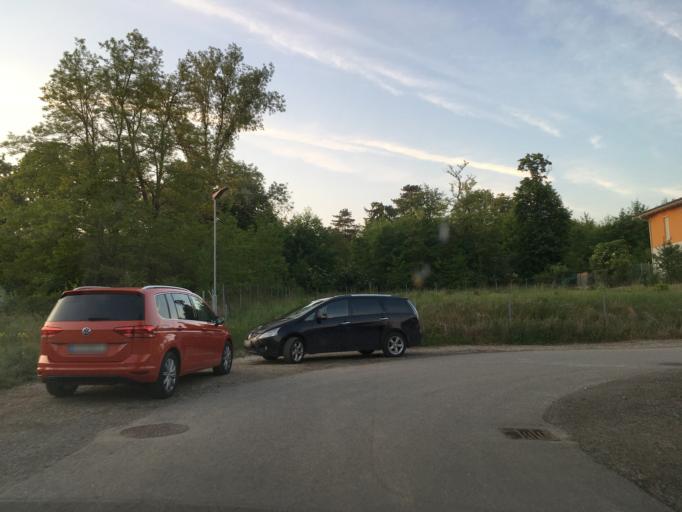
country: AT
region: Lower Austria
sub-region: Politischer Bezirk Korneuburg
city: Stockerau
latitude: 48.3910
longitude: 16.1978
